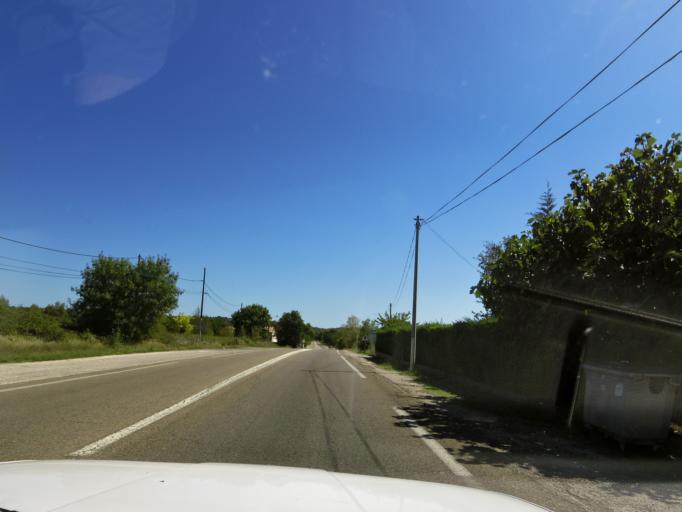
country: FR
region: Languedoc-Roussillon
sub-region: Departement du Gard
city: Saint-Hilaire-de-Brethmas
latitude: 44.0861
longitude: 4.1110
